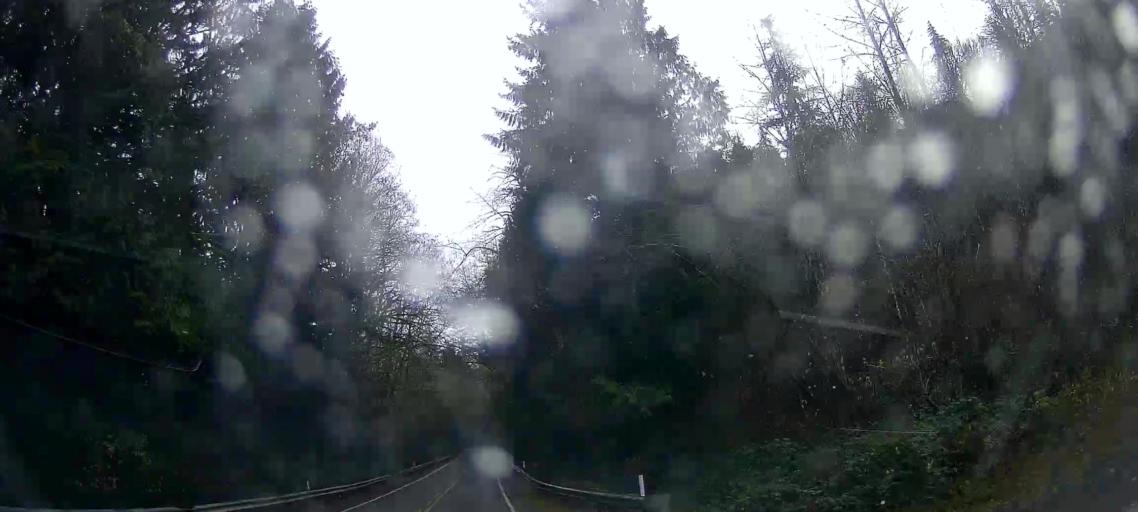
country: US
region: Washington
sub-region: Snohomish County
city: Darrington
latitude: 48.5278
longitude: -121.7793
